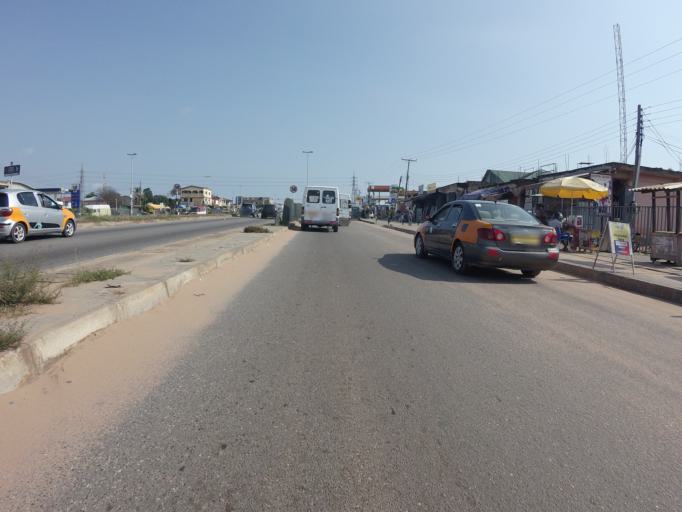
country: GH
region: Greater Accra
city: Gbawe
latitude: 5.6007
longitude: -0.2922
